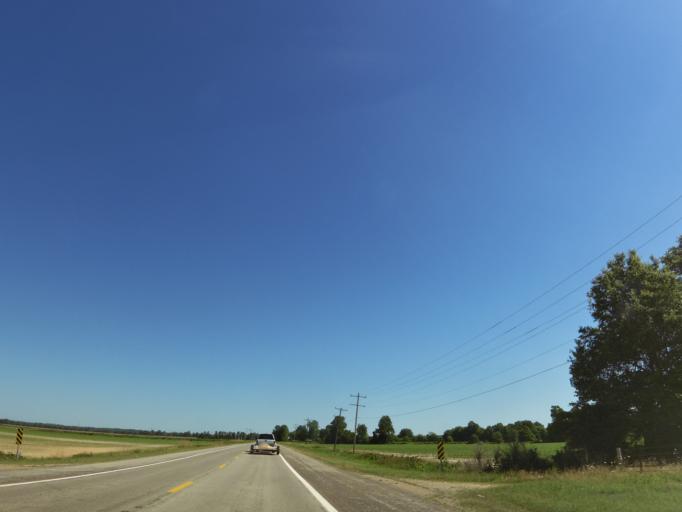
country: US
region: Arkansas
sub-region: Clay County
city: Piggott
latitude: 36.4326
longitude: -90.1473
